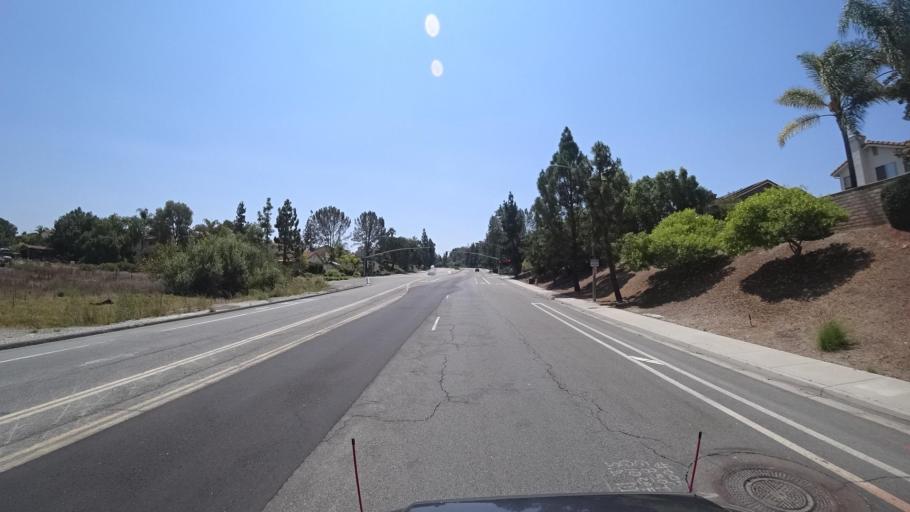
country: US
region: California
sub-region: San Diego County
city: Vista
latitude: 33.2317
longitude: -117.2626
